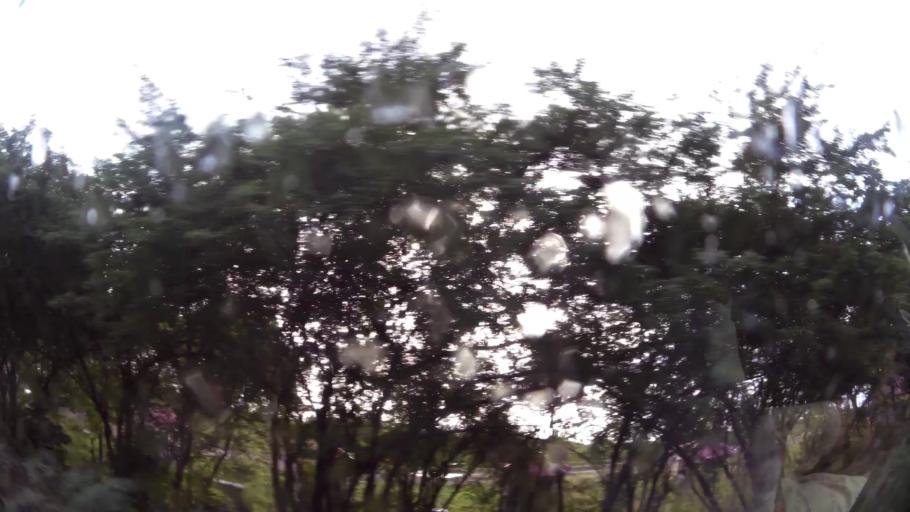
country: DM
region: Saint Paul
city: Mahaut
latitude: 15.3769
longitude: -61.4067
